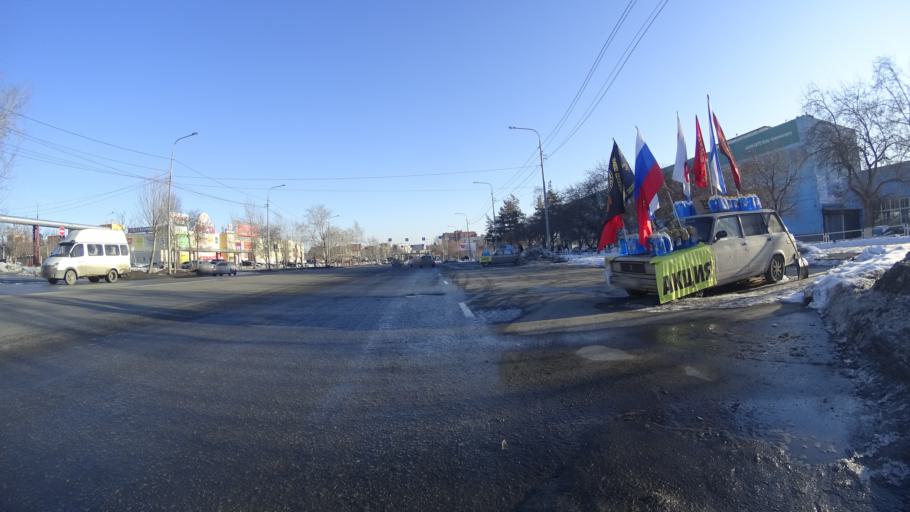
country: RU
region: Chelyabinsk
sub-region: Gorod Chelyabinsk
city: Chelyabinsk
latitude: 55.2048
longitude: 61.3226
